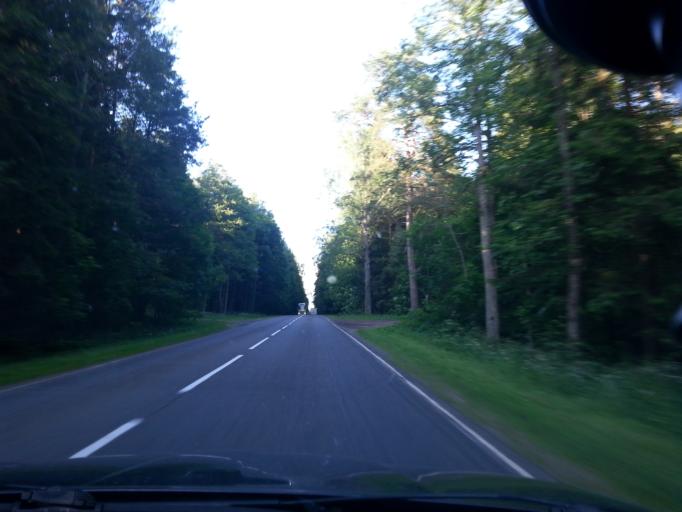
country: BY
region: Minsk
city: Svir
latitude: 54.9065
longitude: 26.4277
